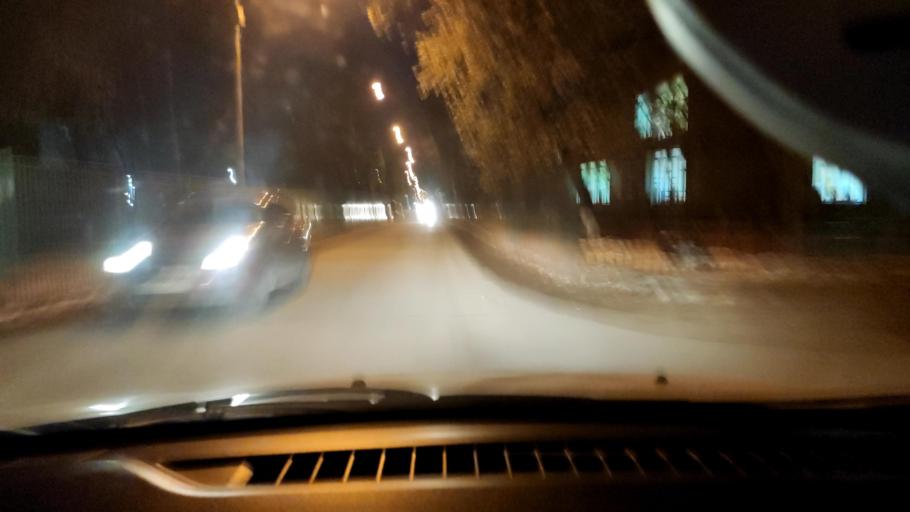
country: RU
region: Perm
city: Kultayevo
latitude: 58.0042
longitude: 55.9528
